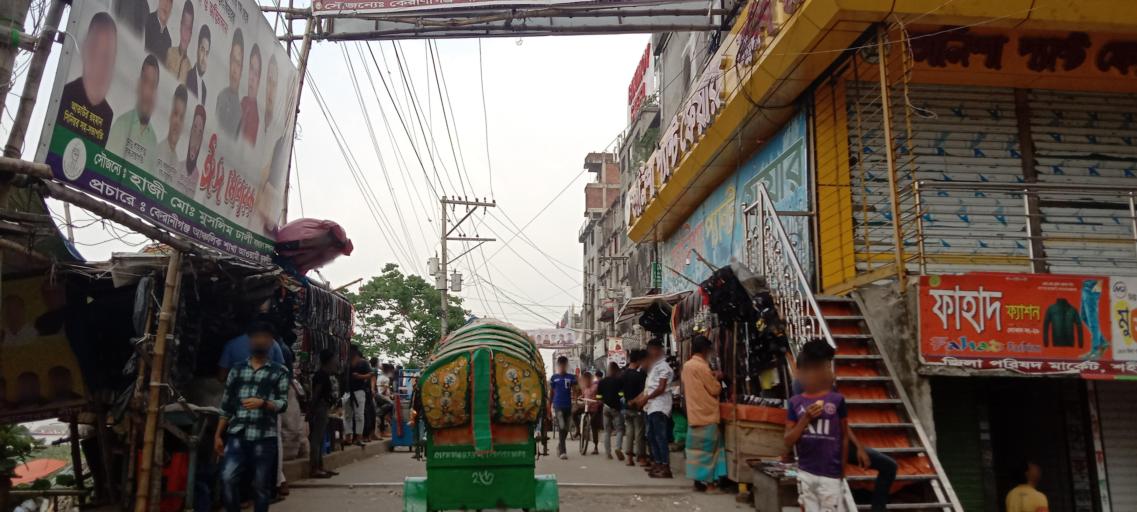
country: BD
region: Dhaka
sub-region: Dhaka
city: Dhaka
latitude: 23.7038
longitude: 90.4073
